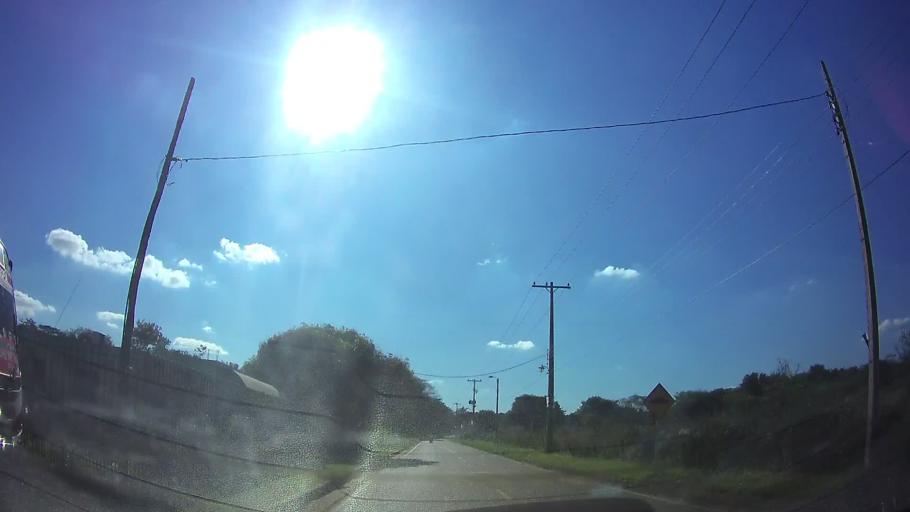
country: PY
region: Central
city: Limpio
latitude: -25.2129
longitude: -57.4776
